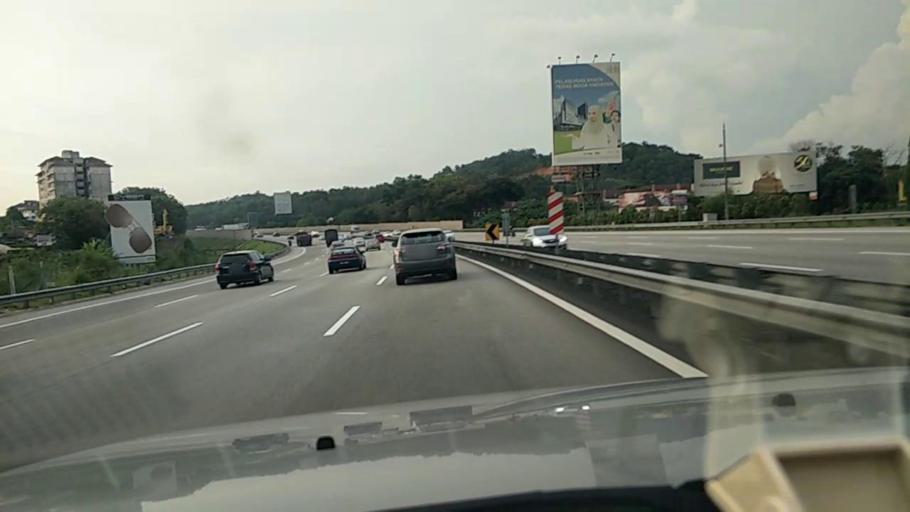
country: MY
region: Selangor
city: Kuang
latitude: 3.2464
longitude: 101.5660
